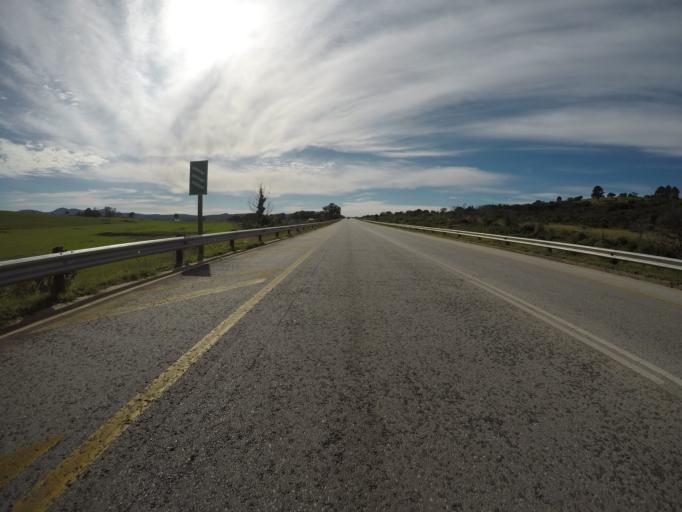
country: ZA
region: Eastern Cape
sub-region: Cacadu District Municipality
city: Jeffrey's Bay
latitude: -33.9012
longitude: 25.1134
